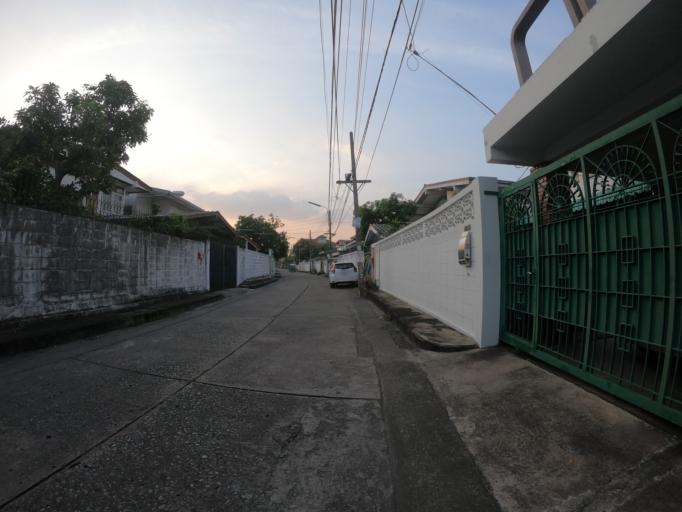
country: TH
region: Bangkok
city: Lat Phrao
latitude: 13.8305
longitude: 100.6073
